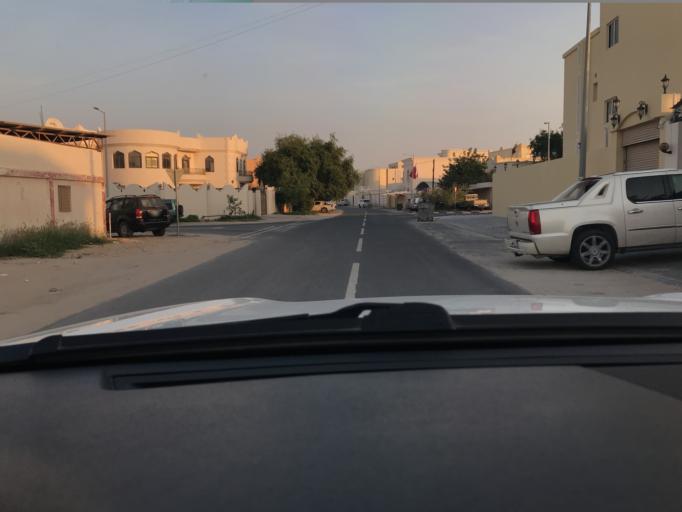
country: QA
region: Baladiyat ad Dawhah
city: Doha
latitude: 25.2520
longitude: 51.5055
